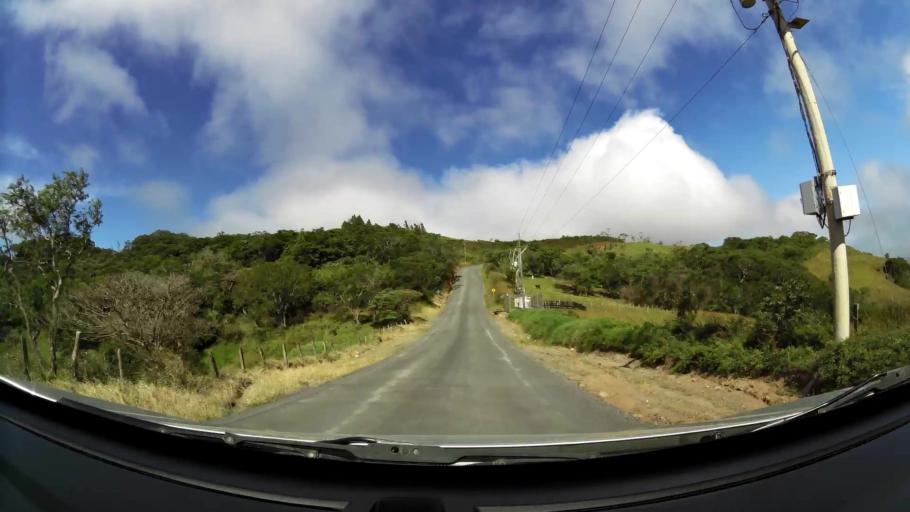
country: CR
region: Guanacaste
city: Juntas
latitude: 10.3394
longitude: -84.8992
